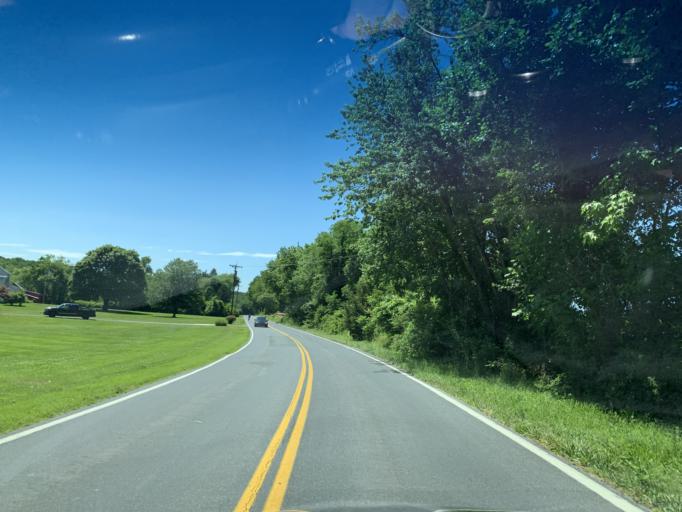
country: US
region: Maryland
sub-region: Harford County
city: Aberdeen
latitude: 39.5566
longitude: -76.1557
